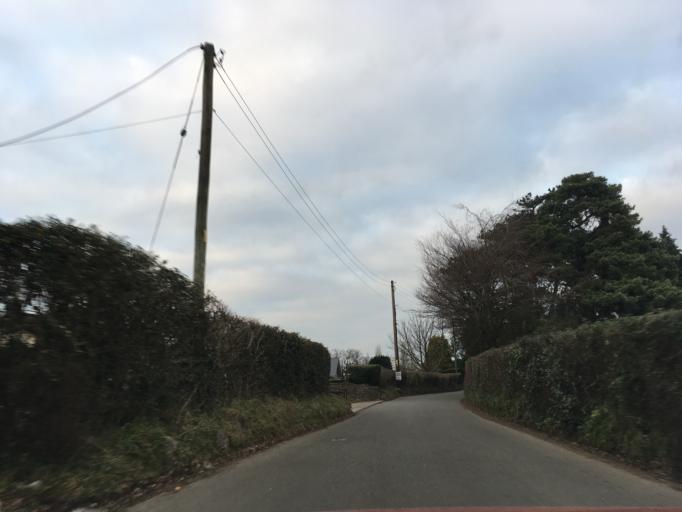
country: GB
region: Wales
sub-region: Newport
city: Marshfield
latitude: 51.5535
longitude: -3.0954
